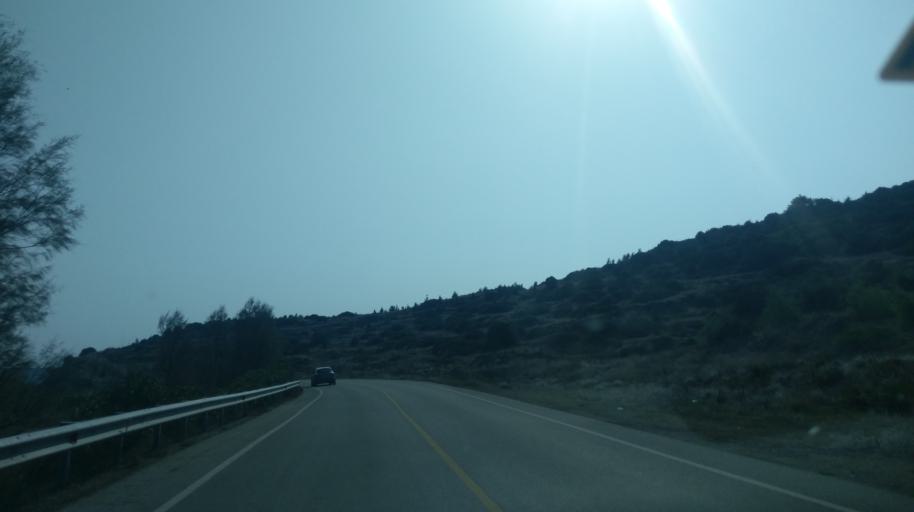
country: CY
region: Ammochostos
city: Leonarisso
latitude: 35.4830
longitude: 34.1043
